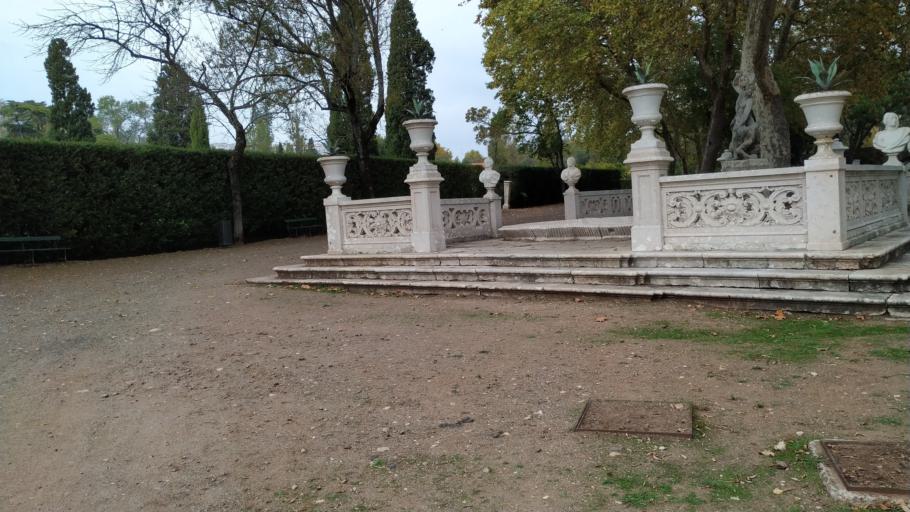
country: PT
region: Lisbon
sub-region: Sintra
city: Queluz
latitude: 38.7510
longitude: -9.2600
